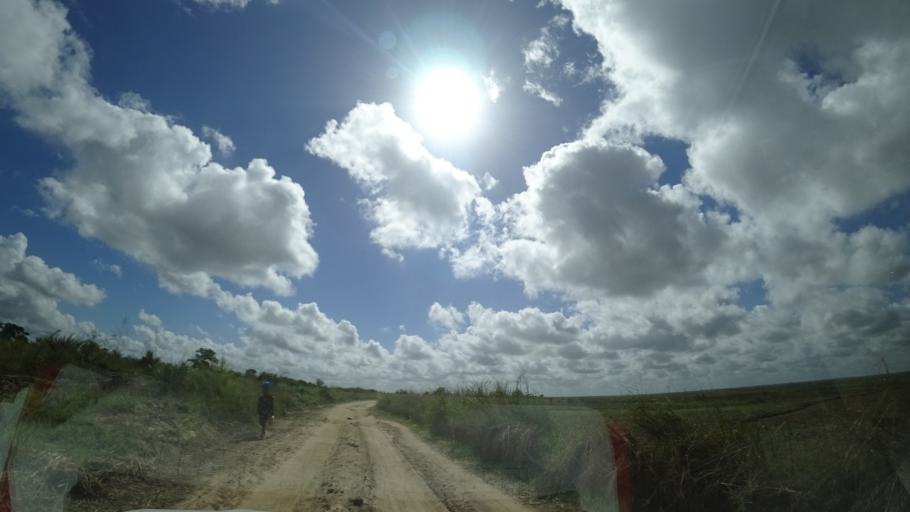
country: MZ
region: Sofala
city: Dondo
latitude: -19.4210
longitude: 34.5638
